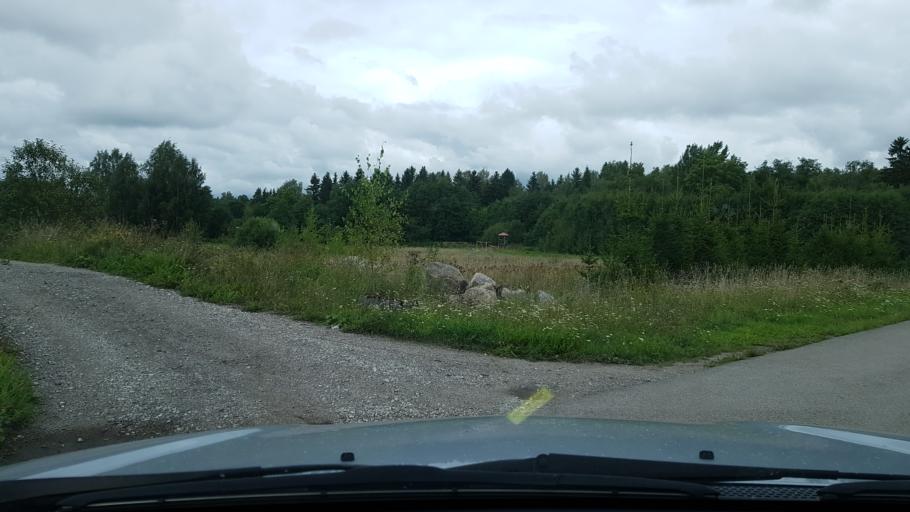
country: EE
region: Harju
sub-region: Rae vald
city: Vaida
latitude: 59.3189
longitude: 24.9417
